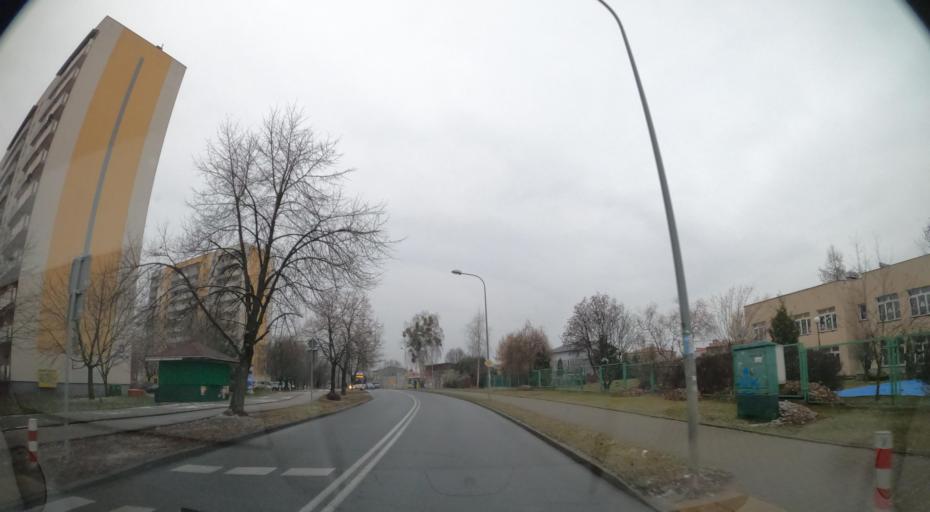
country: PL
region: Masovian Voivodeship
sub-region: Powiat radomski
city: Trablice
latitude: 51.3725
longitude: 21.1299
